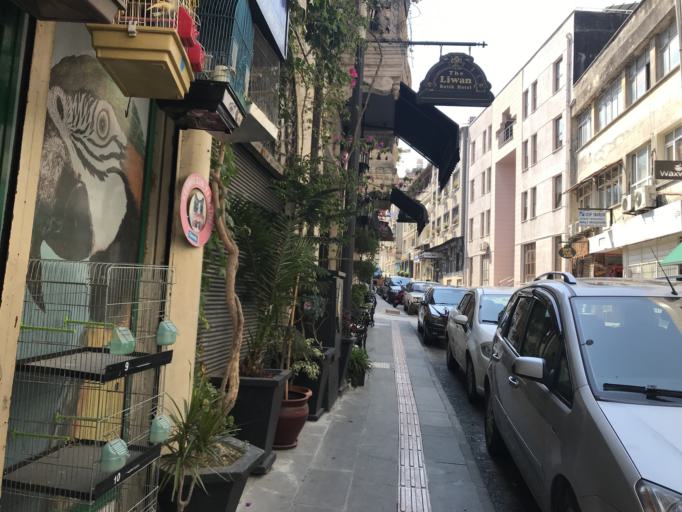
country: TR
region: Hatay
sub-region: Antakya Ilcesi
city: Antakya
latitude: 36.1990
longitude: 36.1608
